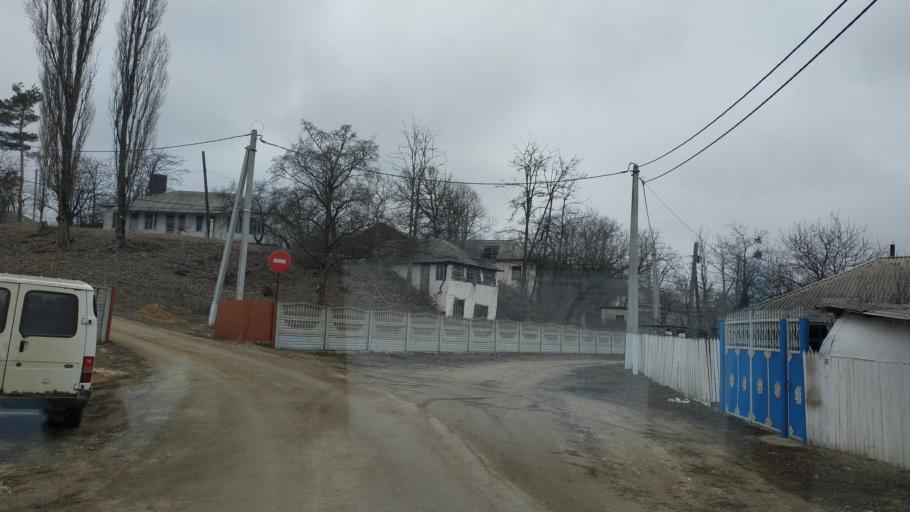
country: MD
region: Hincesti
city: Hincesti
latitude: 46.9806
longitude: 28.4734
